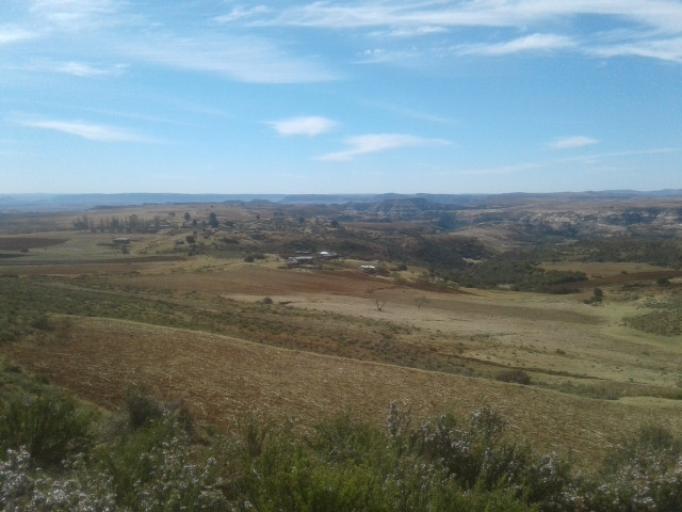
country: LS
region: Maseru
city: Nako
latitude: -29.5439
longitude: 27.6810
